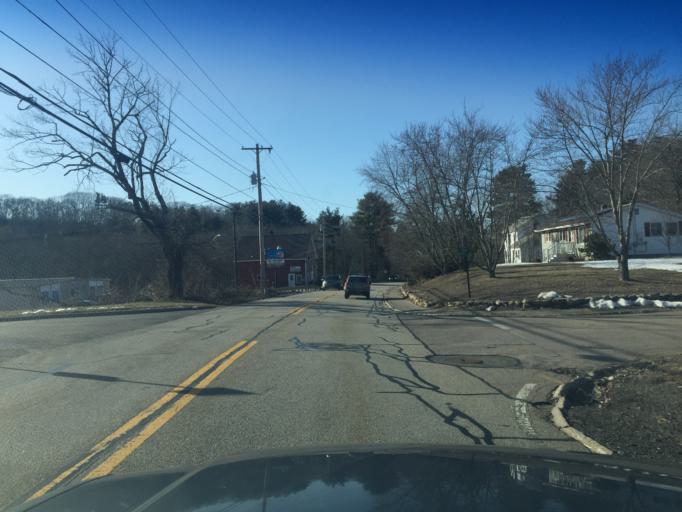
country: US
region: Massachusetts
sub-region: Norfolk County
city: Bellingham
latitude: 42.0825
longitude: -71.4678
